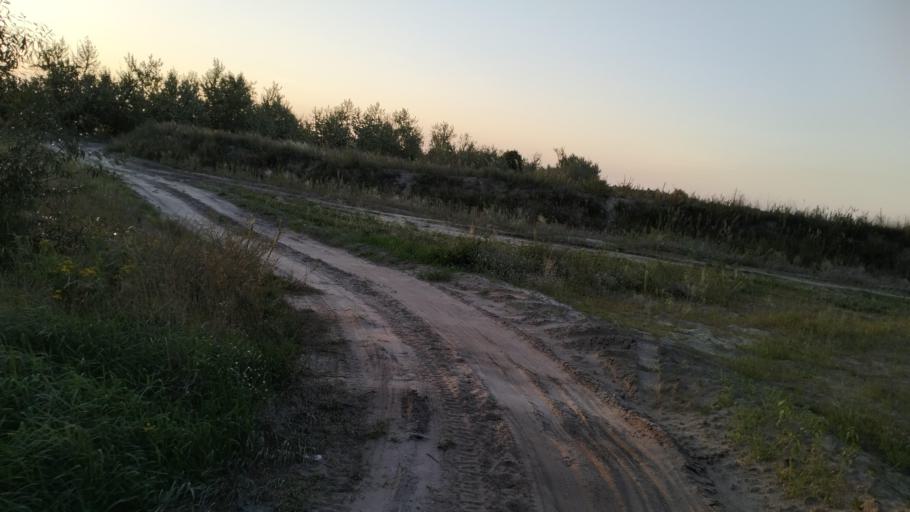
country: BY
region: Brest
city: Davyd-Haradok
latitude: 52.0301
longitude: 27.1949
